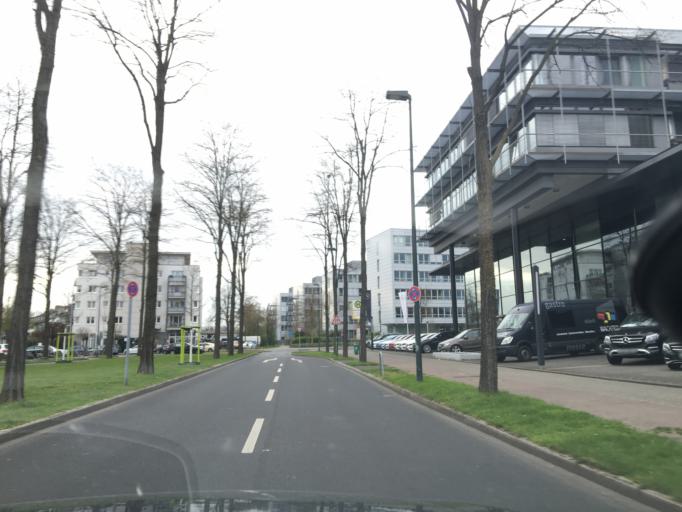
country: DE
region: North Rhine-Westphalia
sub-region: Regierungsbezirk Dusseldorf
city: Dusseldorf
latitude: 51.2495
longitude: 6.7984
